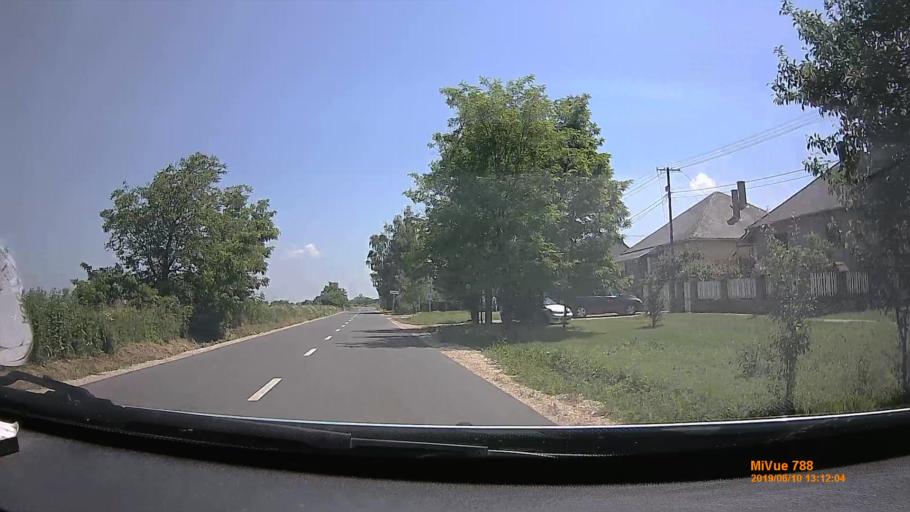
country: HU
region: Borsod-Abauj-Zemplen
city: Hernadnemeti
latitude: 48.0669
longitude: 20.9856
